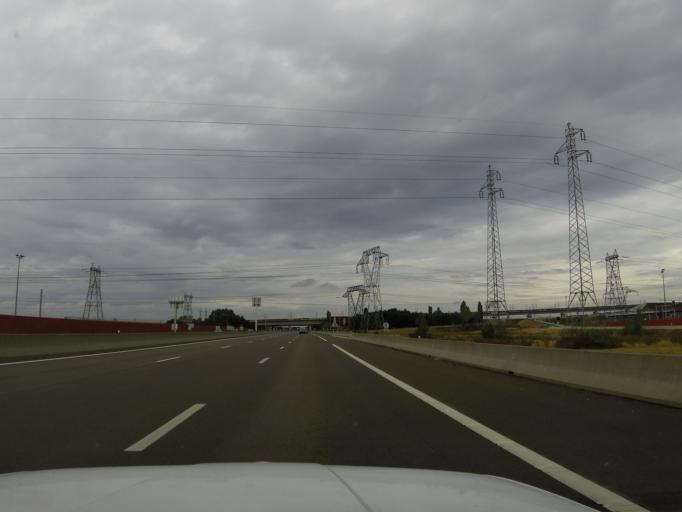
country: FR
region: Rhone-Alpes
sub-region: Departement de l'Ain
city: La Boisse
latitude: 45.8343
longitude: 5.0320
